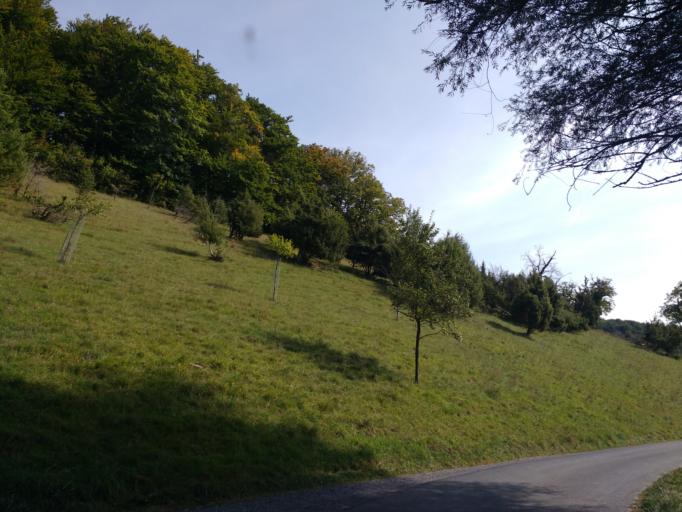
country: DE
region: Hesse
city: Witzenhausen
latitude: 51.3937
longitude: 9.8233
